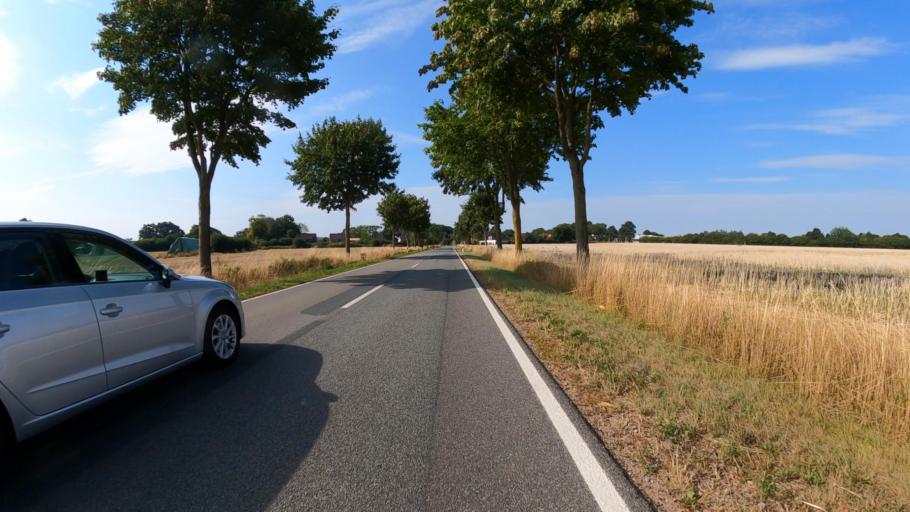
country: DE
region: Schleswig-Holstein
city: Worth
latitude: 53.4719
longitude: 10.4137
